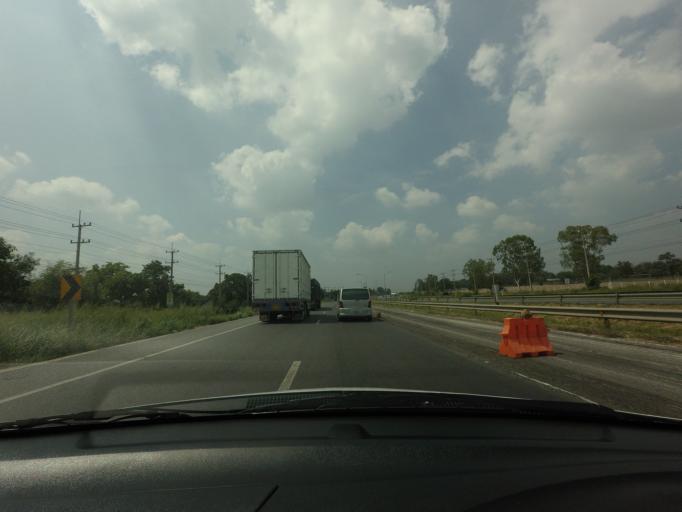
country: TH
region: Nakhon Ratchasima
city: Pak Chong
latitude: 14.6703
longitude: 101.4511
